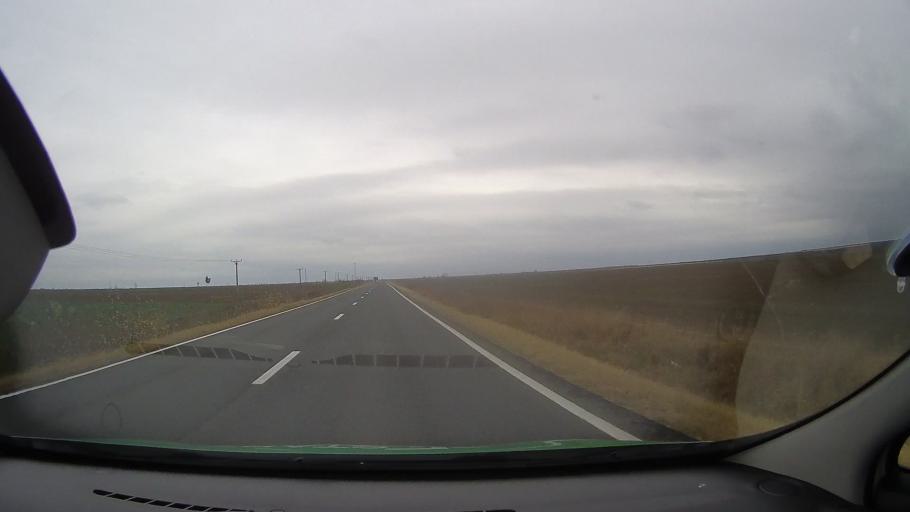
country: RO
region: Constanta
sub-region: Comuna Nicolae Balcescu
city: Nicolae Balcescu
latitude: 44.3787
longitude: 28.4131
